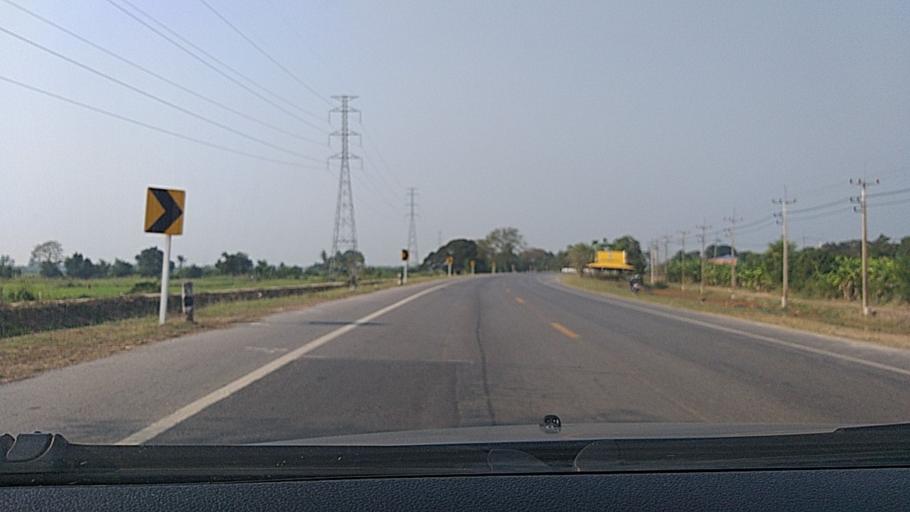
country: TH
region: Sing Buri
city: Tha Chang
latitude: 14.7235
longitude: 100.4303
